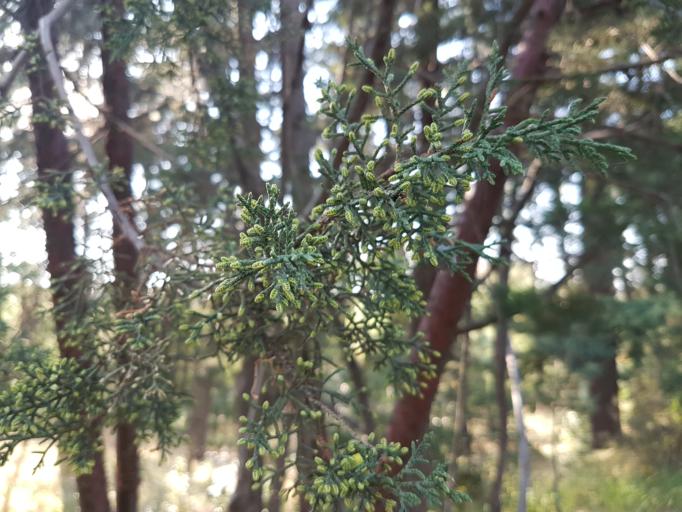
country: ES
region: Madrid
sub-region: Provincia de Madrid
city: Tetuan de las Victorias
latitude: 40.4505
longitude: -3.7226
